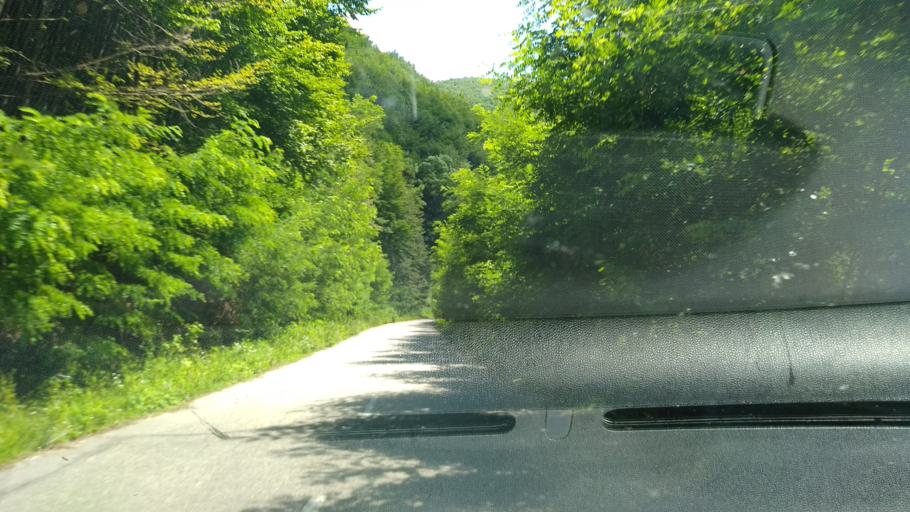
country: RO
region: Hunedoara
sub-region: Comuna Orastioara de Sus
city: Orastioara de Sus
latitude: 45.6452
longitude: 23.1940
